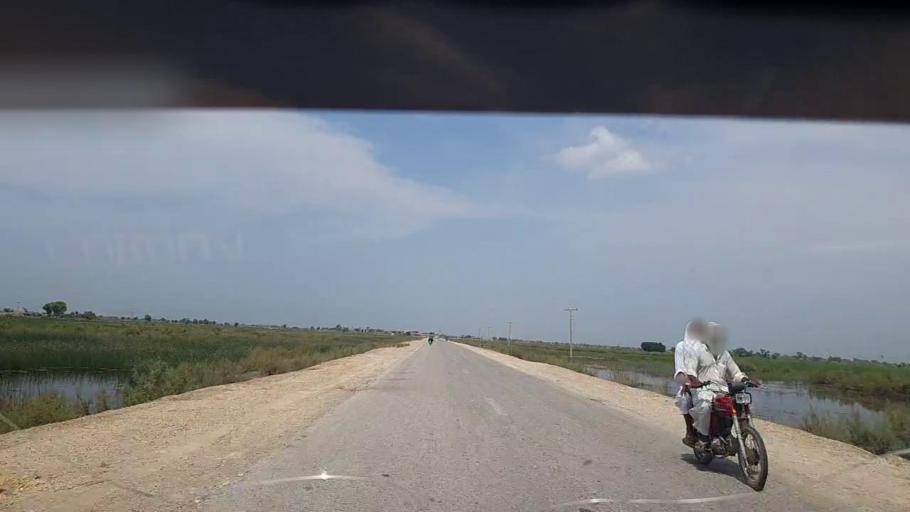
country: PK
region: Sindh
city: Thul
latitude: 28.1916
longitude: 68.7948
